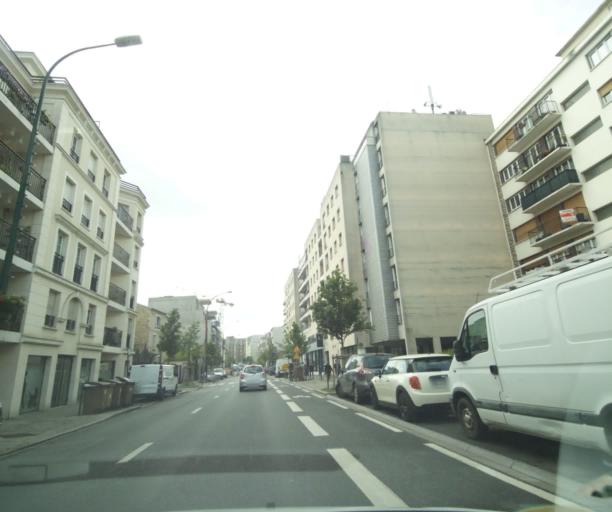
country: FR
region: Ile-de-France
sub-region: Departement des Hauts-de-Seine
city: Colombes
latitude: 48.9165
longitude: 2.2527
